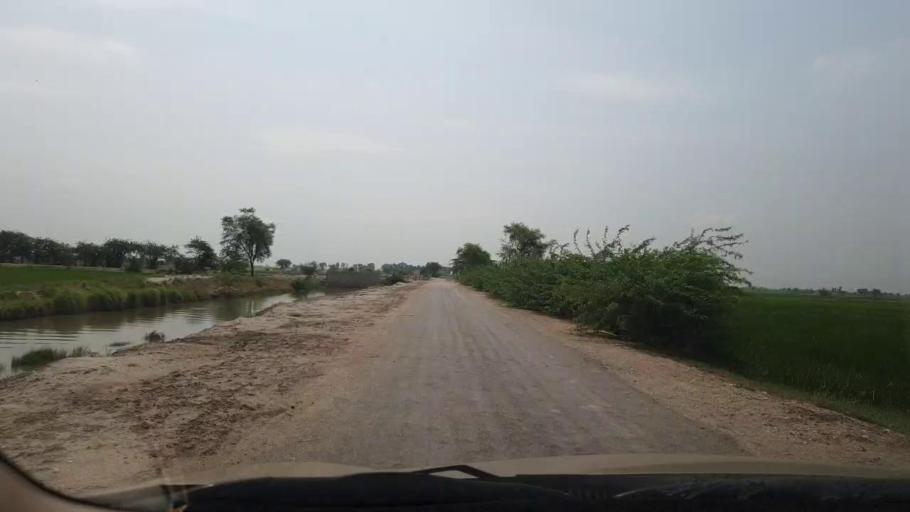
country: PK
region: Sindh
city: Goth Garelo
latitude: 27.5115
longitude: 68.1087
